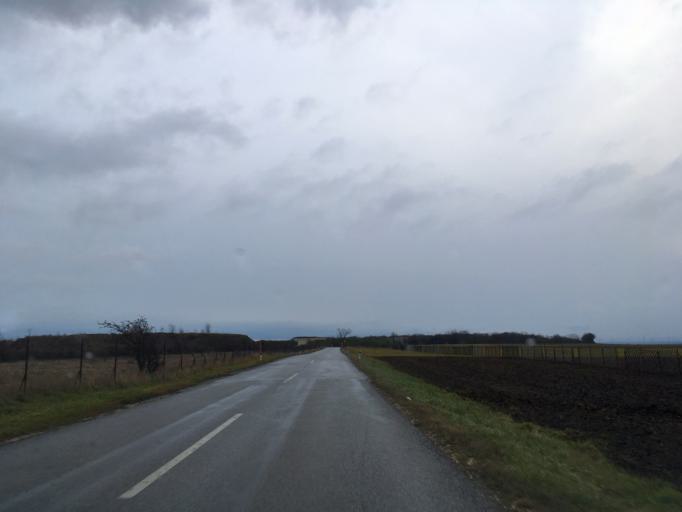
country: AT
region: Lower Austria
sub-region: Politischer Bezirk Wien-Umgebung
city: Rauchenwarth
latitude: 48.0722
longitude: 16.5333
